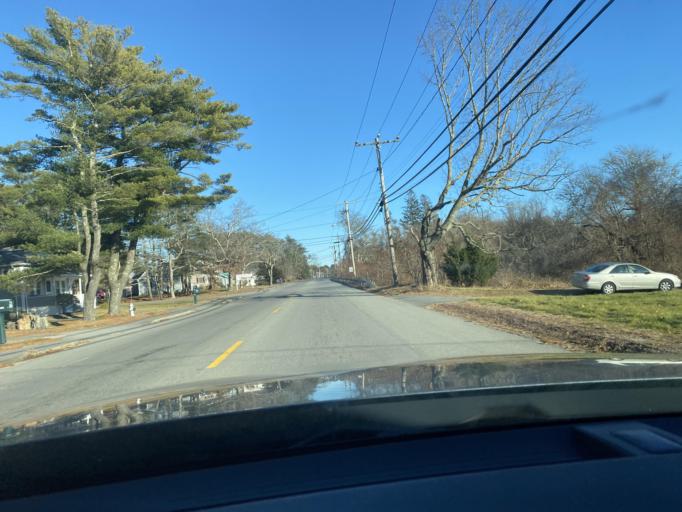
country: US
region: Massachusetts
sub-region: Plymouth County
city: Wareham Center
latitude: 41.7692
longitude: -70.7171
